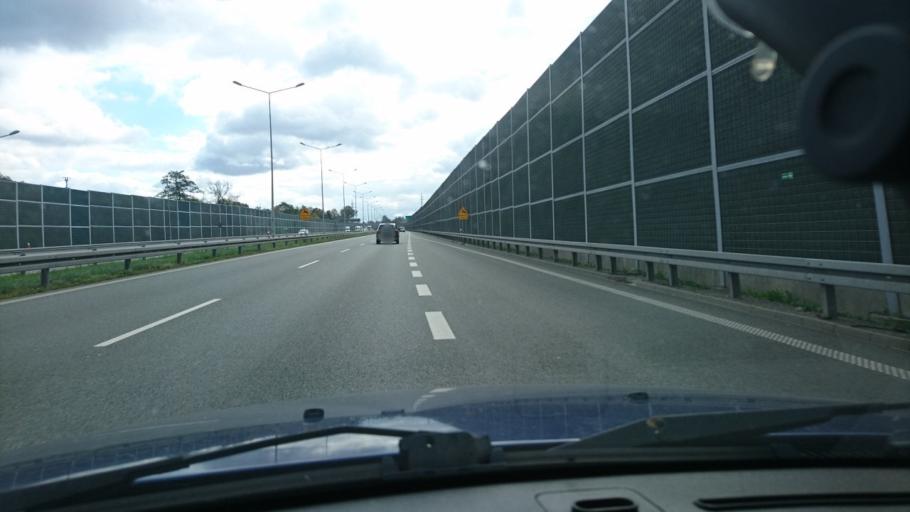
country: PL
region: Silesian Voivodeship
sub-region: Powiat bielski
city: Bystra
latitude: 49.7818
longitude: 19.0707
